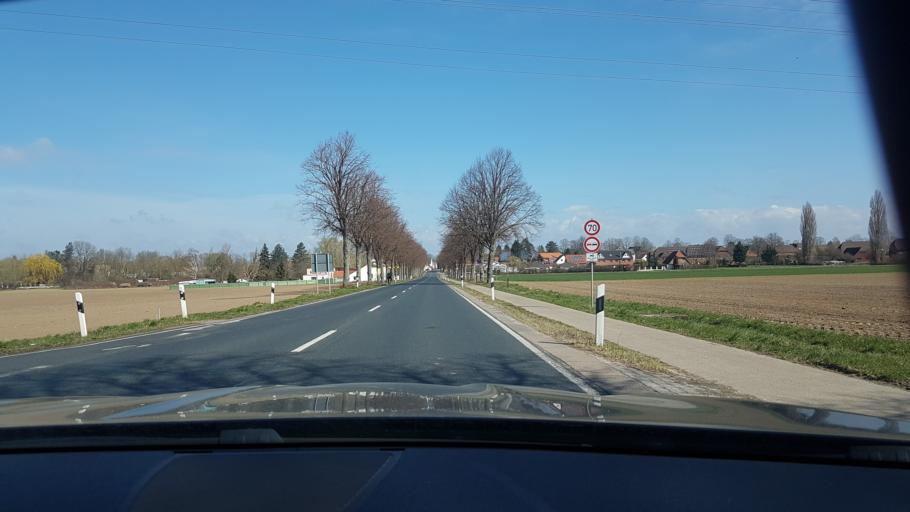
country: DE
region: Lower Saxony
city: Pattensen
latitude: 52.2543
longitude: 9.7570
